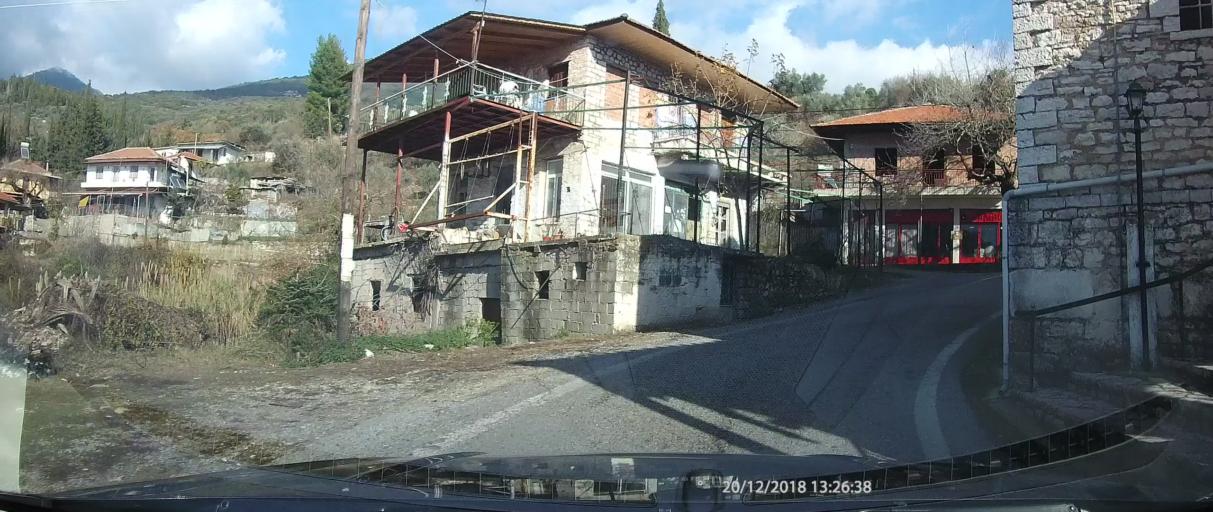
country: GR
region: West Greece
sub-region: Nomos Aitolias kai Akarnanias
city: Paravola
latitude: 38.6308
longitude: 21.5636
